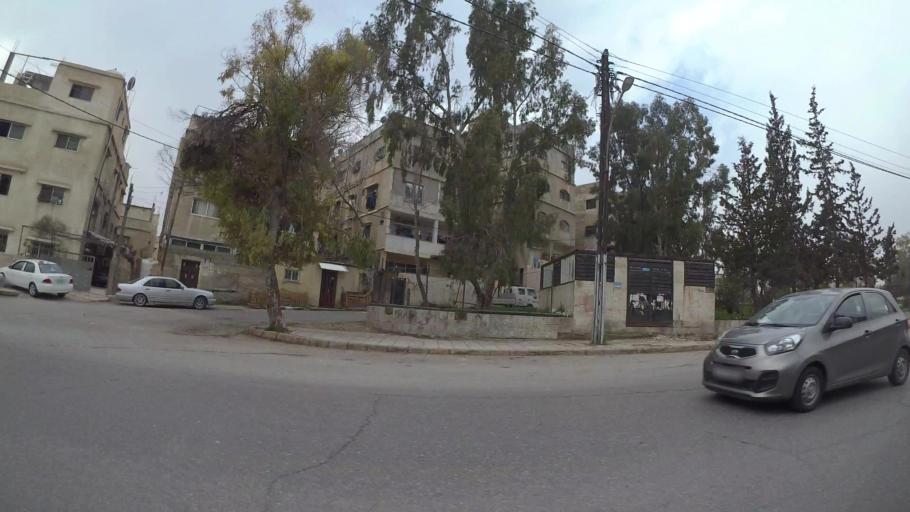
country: JO
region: Amman
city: Amman
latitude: 31.9624
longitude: 35.9382
